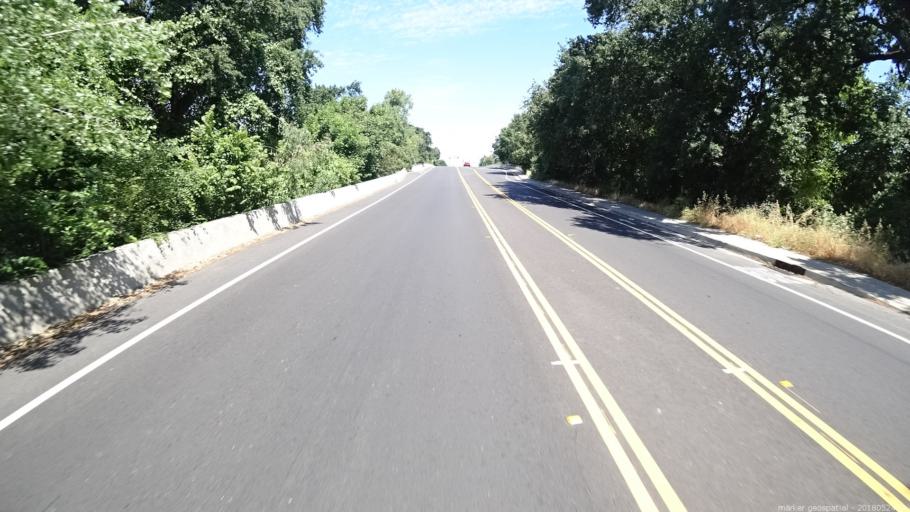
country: US
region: California
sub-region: Sacramento County
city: Sacramento
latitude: 38.6033
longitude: -121.4754
